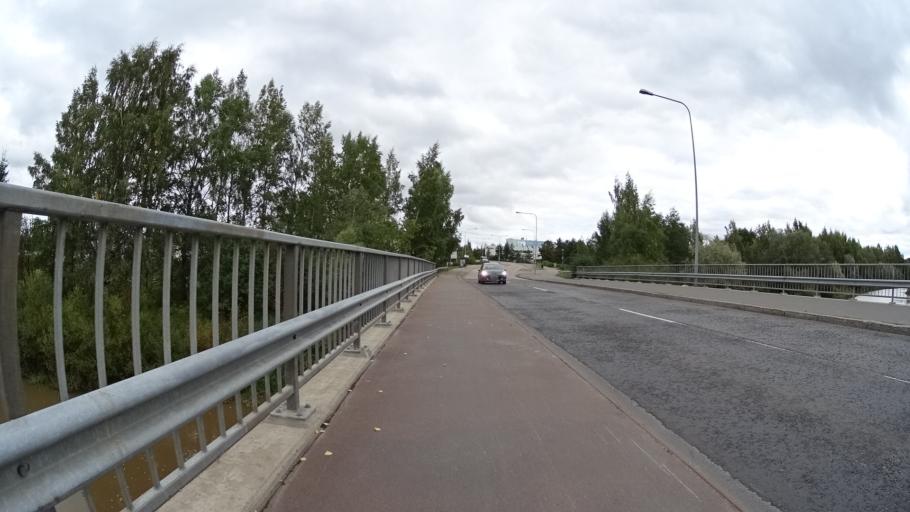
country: FI
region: Uusimaa
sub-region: Helsinki
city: Helsinki
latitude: 60.2401
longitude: 24.9784
